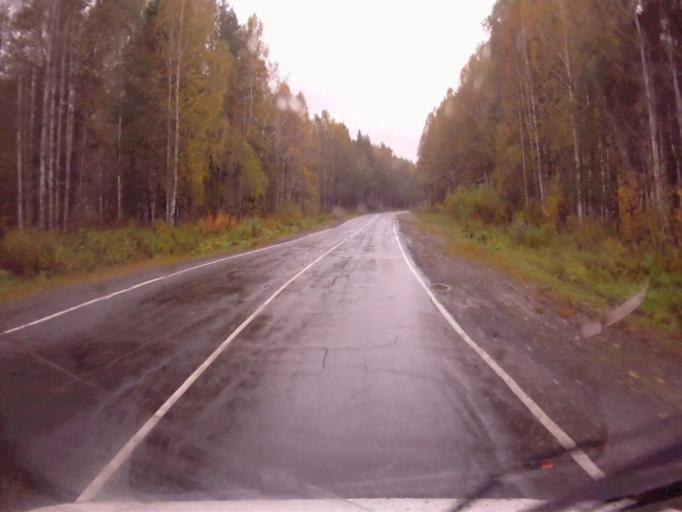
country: RU
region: Chelyabinsk
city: Verkhniy Ufaley
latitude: 55.9532
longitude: 60.3935
